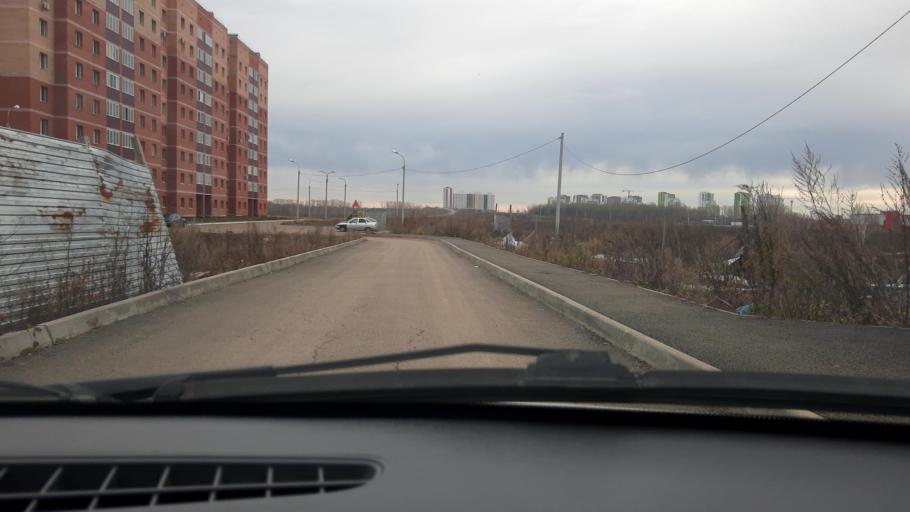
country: RU
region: Bashkortostan
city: Mikhaylovka
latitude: 54.7125
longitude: 55.8458
